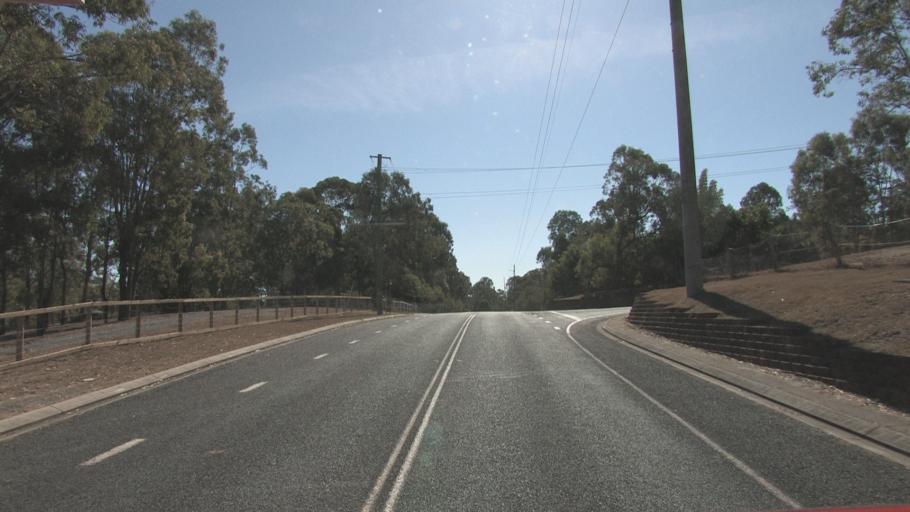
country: AU
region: Queensland
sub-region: Logan
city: Cedar Vale
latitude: -27.8705
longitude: 153.0176
